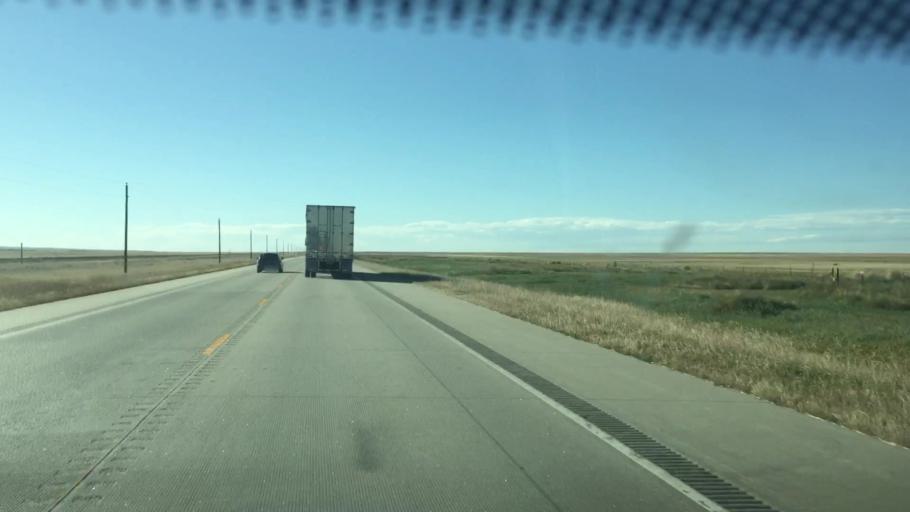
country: US
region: Colorado
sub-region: Kiowa County
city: Eads
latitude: 38.8320
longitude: -103.0493
